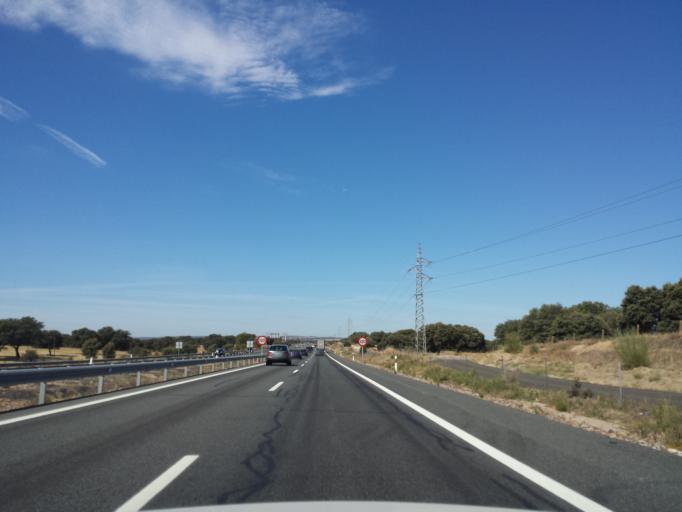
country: ES
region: Castille-La Mancha
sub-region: Province of Toledo
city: Alcanizo
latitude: 39.9202
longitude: -5.0454
